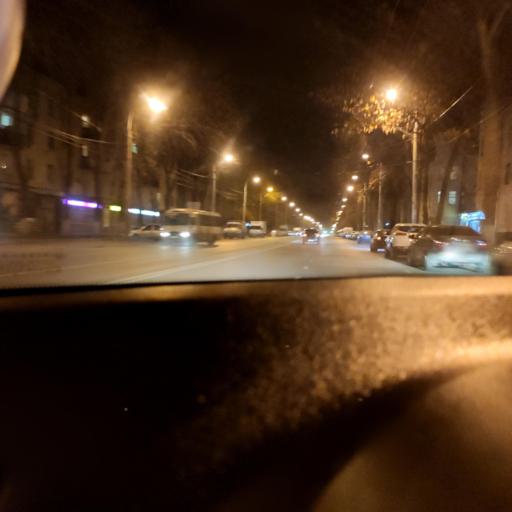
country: RU
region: Samara
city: Petra-Dubrava
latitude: 53.2329
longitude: 50.2754
